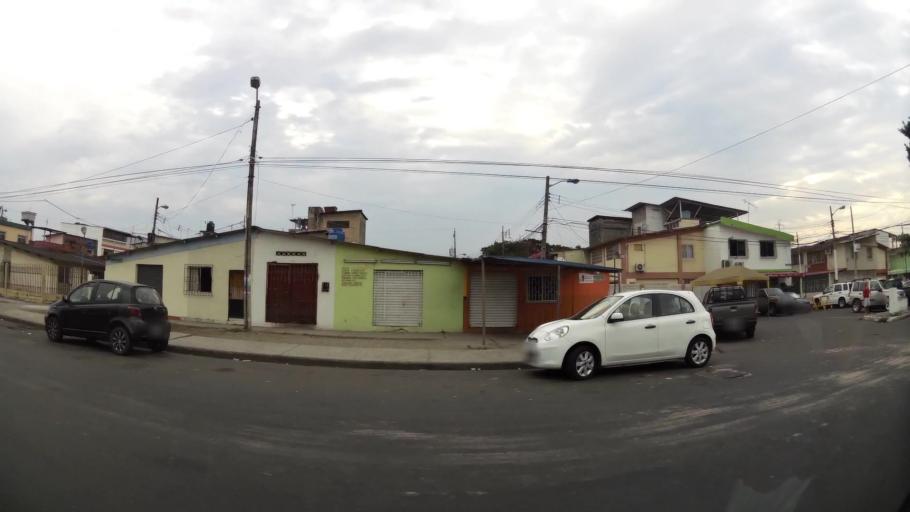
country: EC
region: Guayas
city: Guayaquil
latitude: -2.2381
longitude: -79.8874
